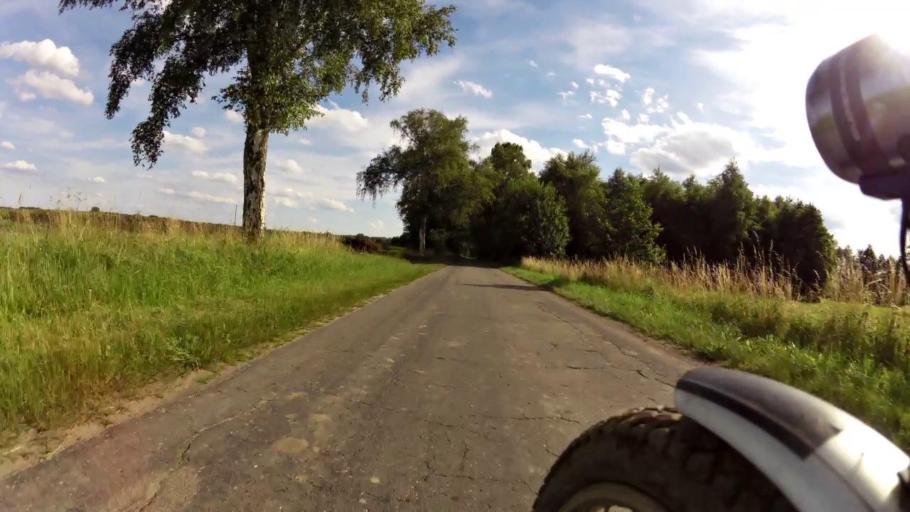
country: PL
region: West Pomeranian Voivodeship
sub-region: Powiat lobeski
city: Wegorzyno
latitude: 53.5489
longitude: 15.4755
